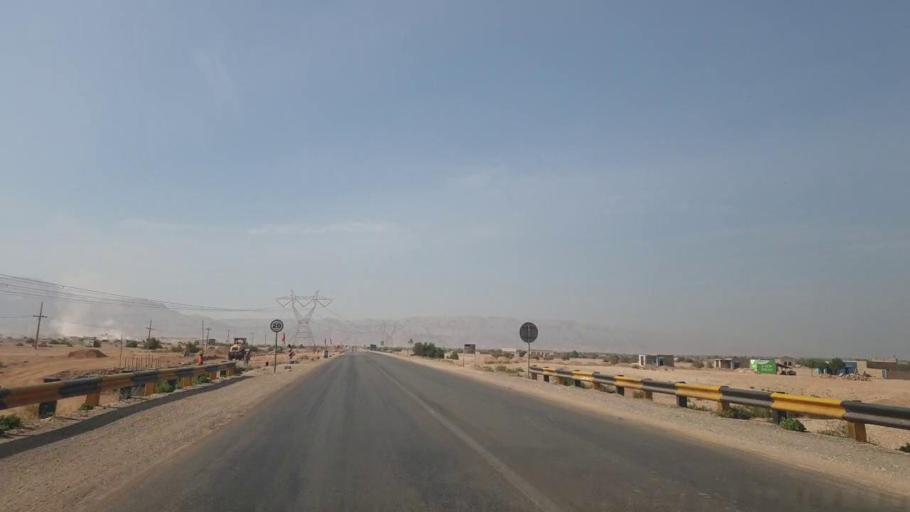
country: PK
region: Sindh
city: Sehwan
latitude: 26.2073
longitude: 67.9284
